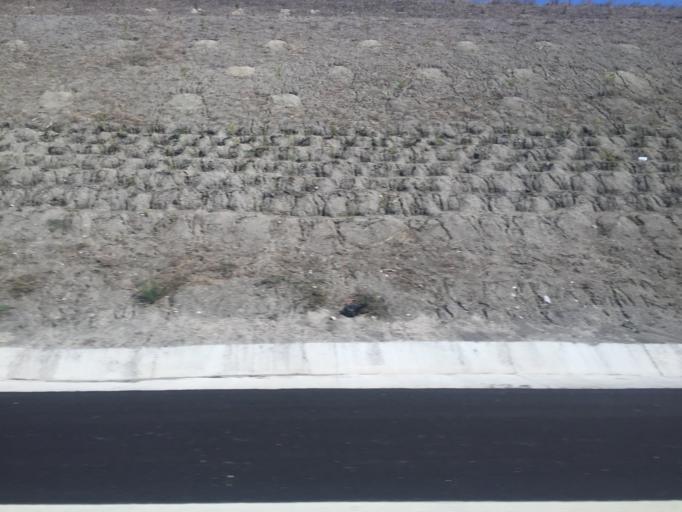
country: TR
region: Bursa
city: Mahmudiye
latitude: 40.2564
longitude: 28.7056
